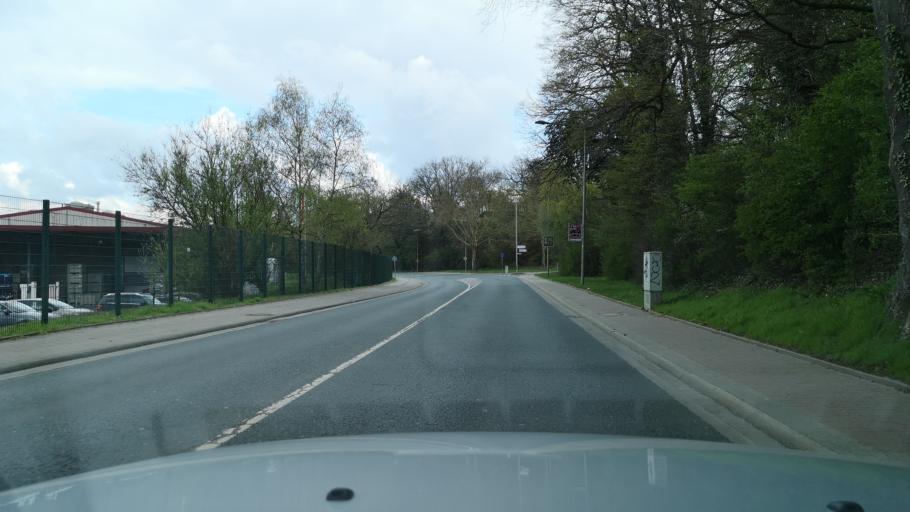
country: DE
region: North Rhine-Westphalia
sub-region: Regierungsbezirk Arnsberg
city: Menden
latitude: 51.4259
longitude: 7.8167
